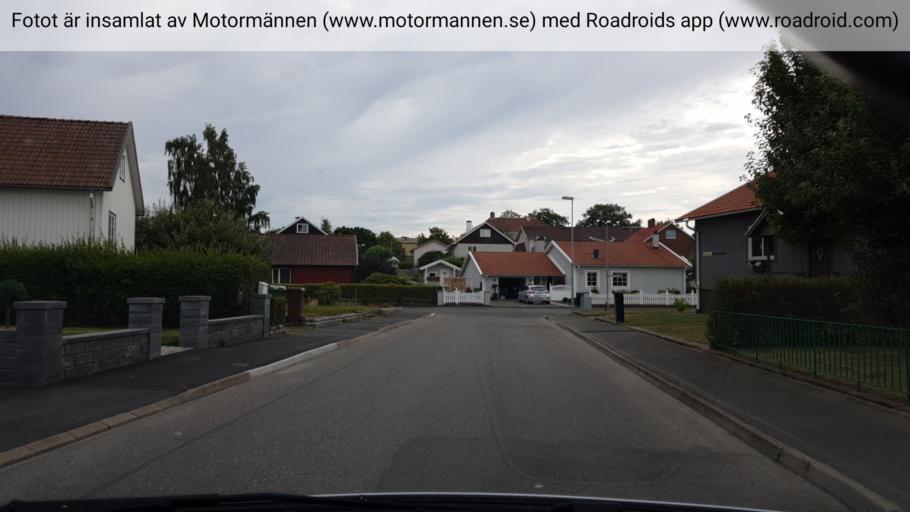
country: SE
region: Vaestra Goetaland
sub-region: Skovde Kommun
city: Skoevde
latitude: 58.3897
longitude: 13.8710
